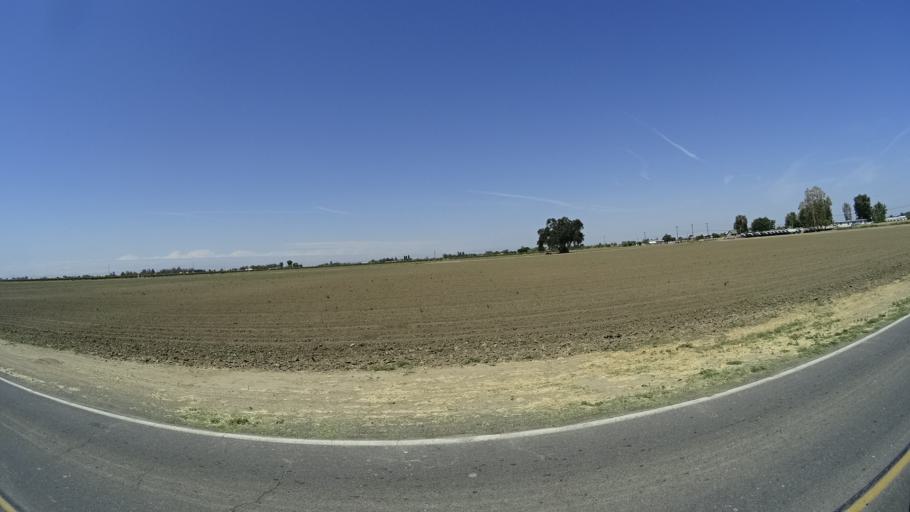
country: US
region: California
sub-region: Kings County
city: Lemoore
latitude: 36.2531
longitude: -119.7628
